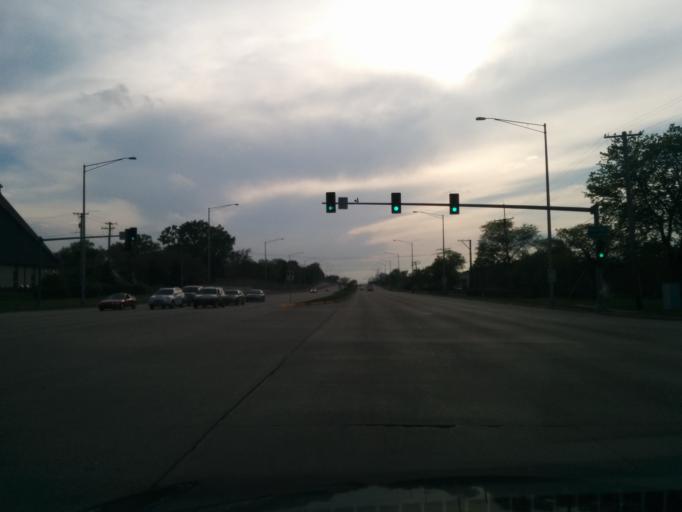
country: US
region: Illinois
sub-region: DuPage County
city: Lombard
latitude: 41.9048
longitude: -88.0173
